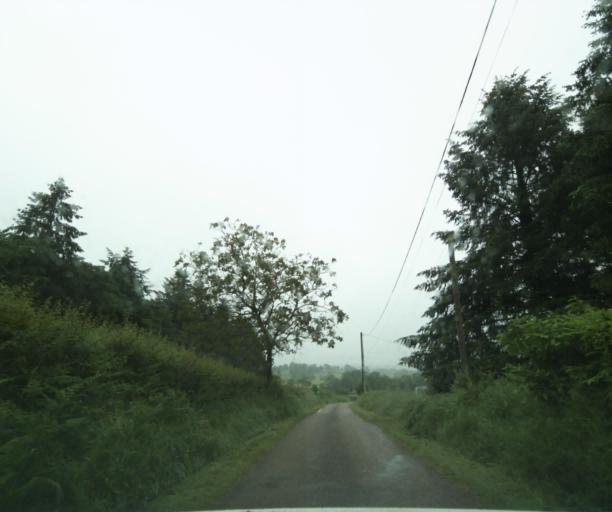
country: FR
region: Bourgogne
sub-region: Departement de Saone-et-Loire
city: Charolles
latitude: 46.4244
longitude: 4.3694
